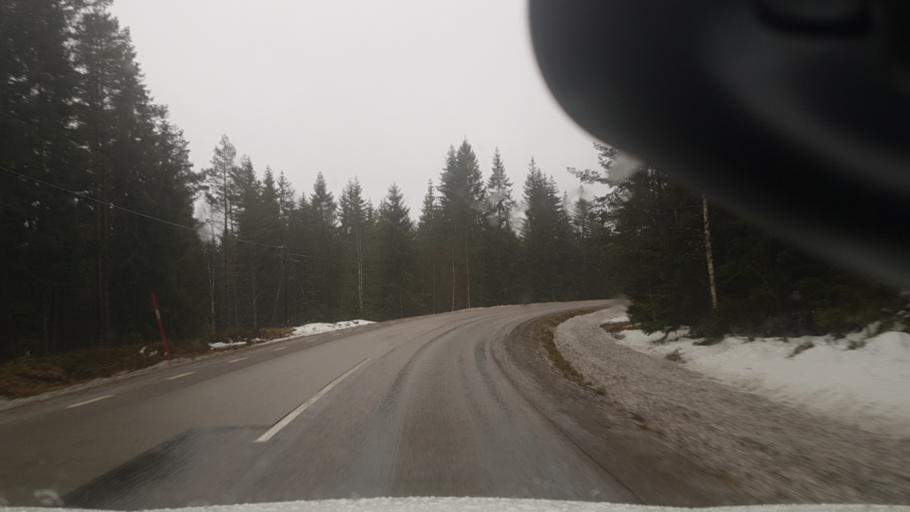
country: SE
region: Vaermland
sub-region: Arjangs Kommun
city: Arjaeng
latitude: 59.5552
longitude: 12.1723
